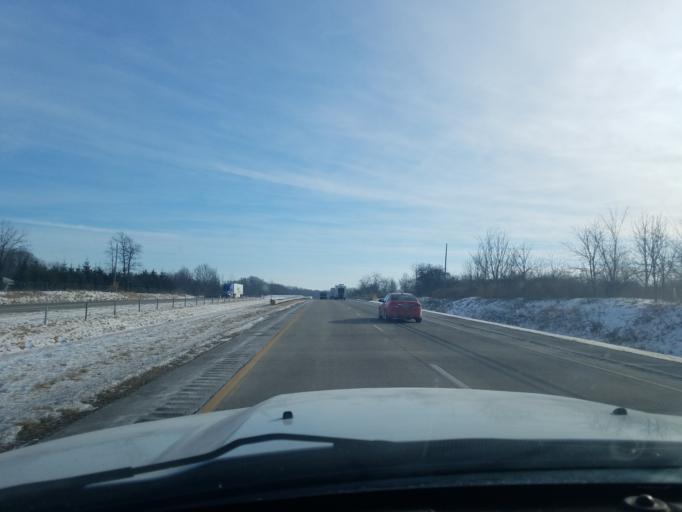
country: US
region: Indiana
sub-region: Grant County
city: Upland
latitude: 40.4535
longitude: -85.5492
